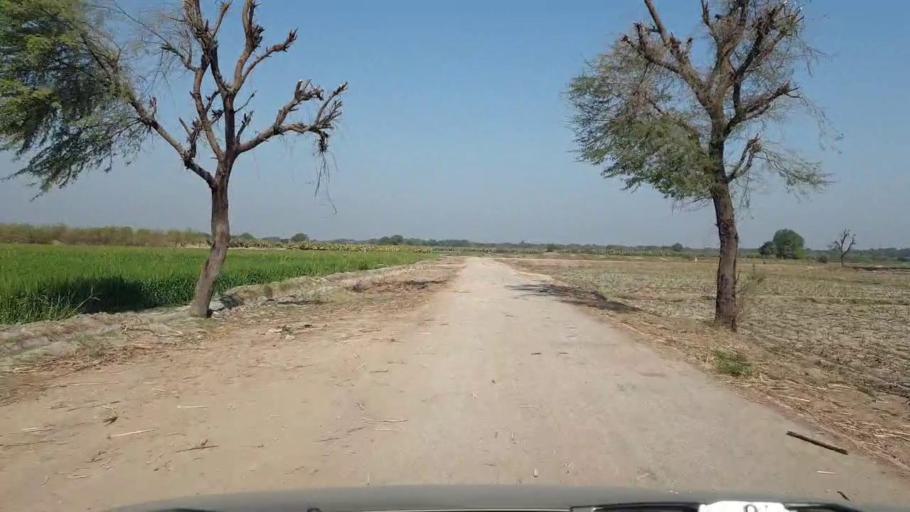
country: PK
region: Sindh
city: Tando Jam
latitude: 25.4385
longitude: 68.6176
